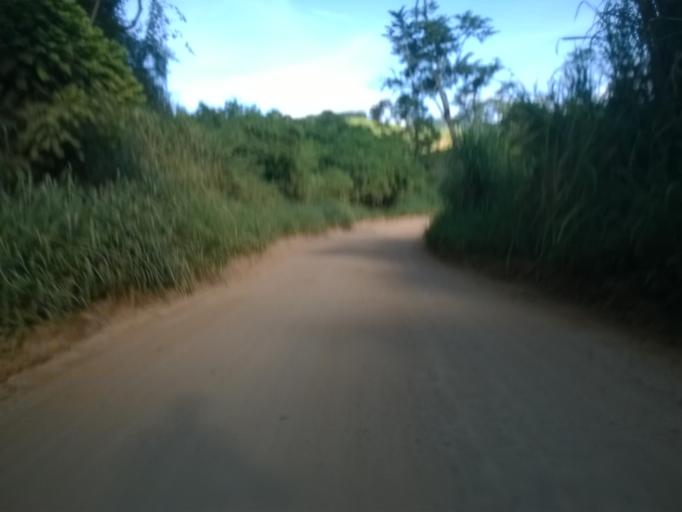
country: BR
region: Minas Gerais
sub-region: Uba
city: Uba
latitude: -21.0848
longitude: -43.0024
